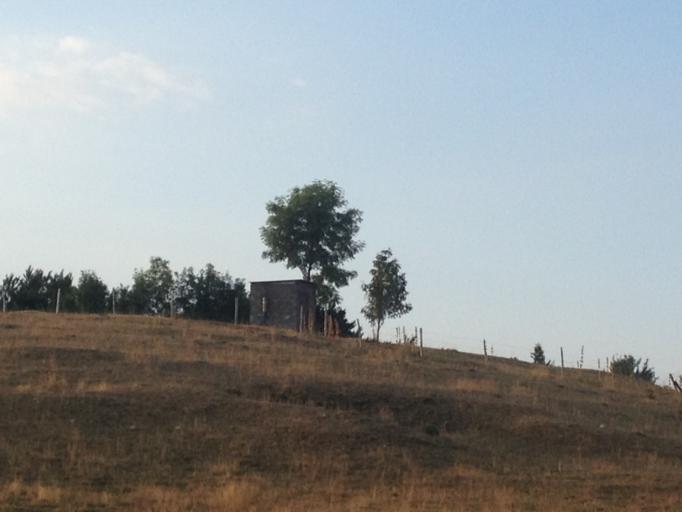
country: FR
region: Rhone-Alpes
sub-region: Departement de la Haute-Savoie
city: Collonges-sous-Saleve
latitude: 46.1382
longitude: 6.1813
